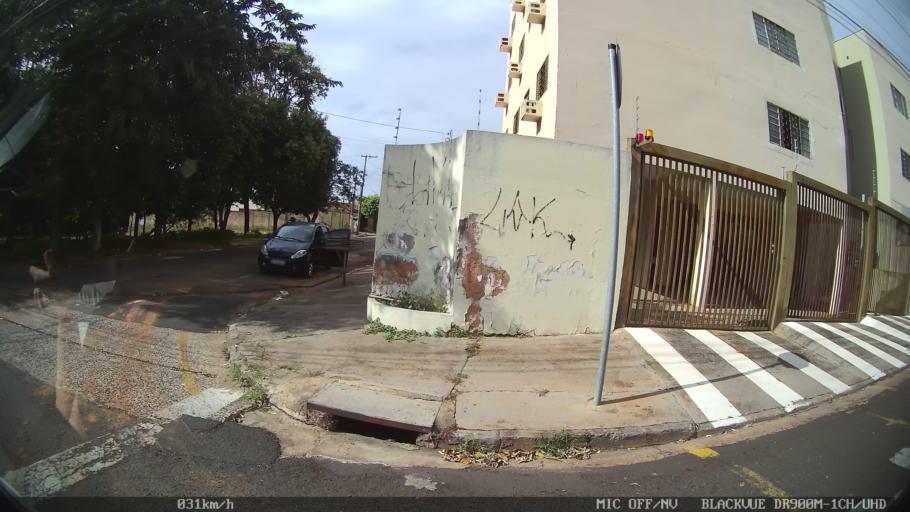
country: BR
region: Sao Paulo
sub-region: Sao Jose Do Rio Preto
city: Sao Jose do Rio Preto
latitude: -20.8373
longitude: -49.3726
